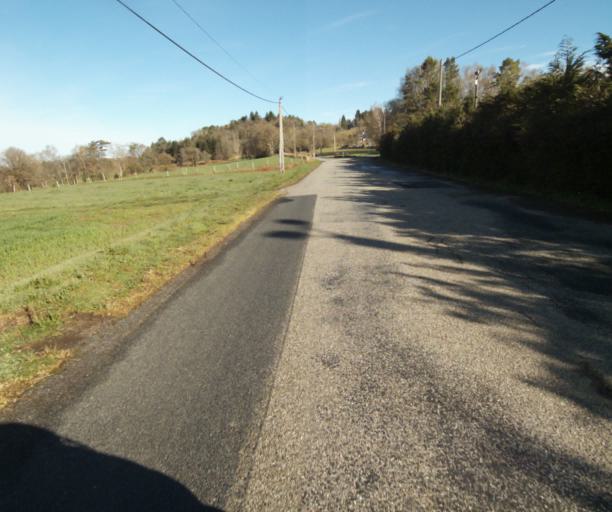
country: FR
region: Limousin
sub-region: Departement de la Correze
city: Laguenne
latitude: 45.2718
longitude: 1.8652
